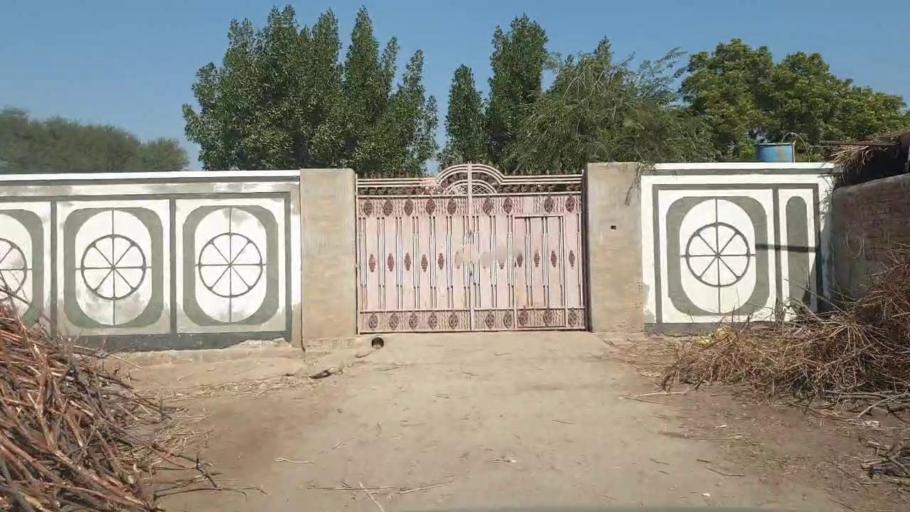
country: PK
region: Sindh
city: Tando Jam
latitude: 25.2980
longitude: 68.6307
